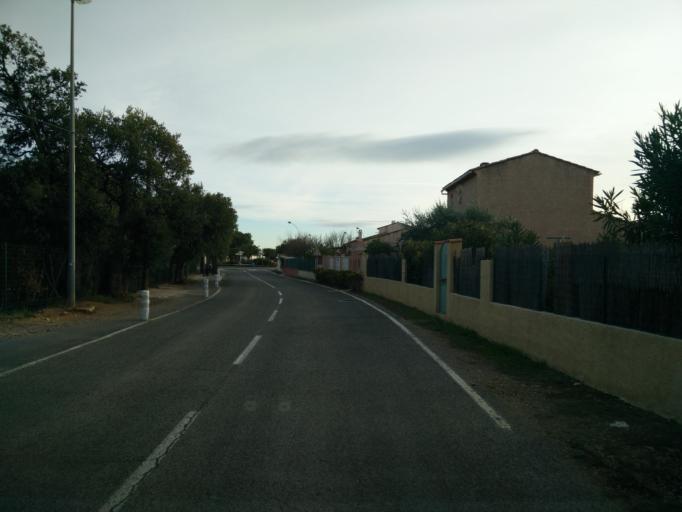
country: FR
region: Provence-Alpes-Cote d'Azur
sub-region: Departement du Var
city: La Londe-les-Maures
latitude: 43.1329
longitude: 6.2297
